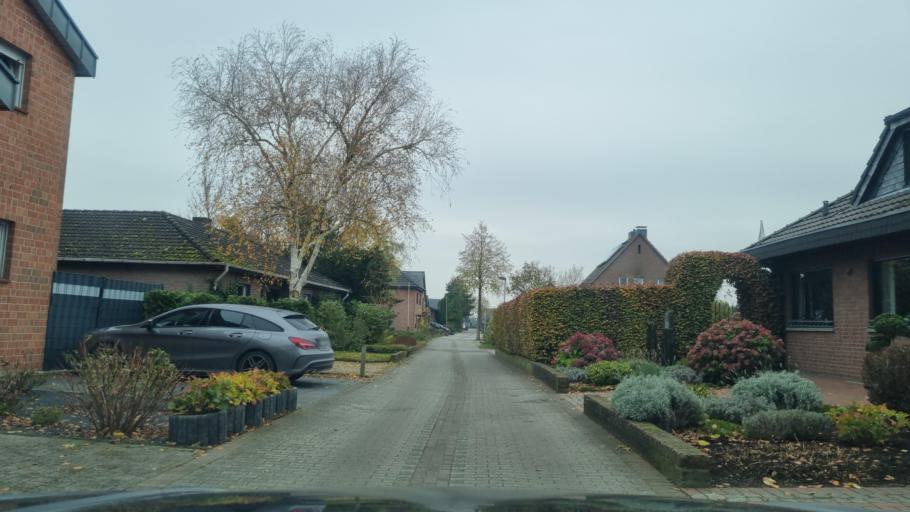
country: DE
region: North Rhine-Westphalia
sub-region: Regierungsbezirk Dusseldorf
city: Kranenburg
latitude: 51.7887
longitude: 6.0634
